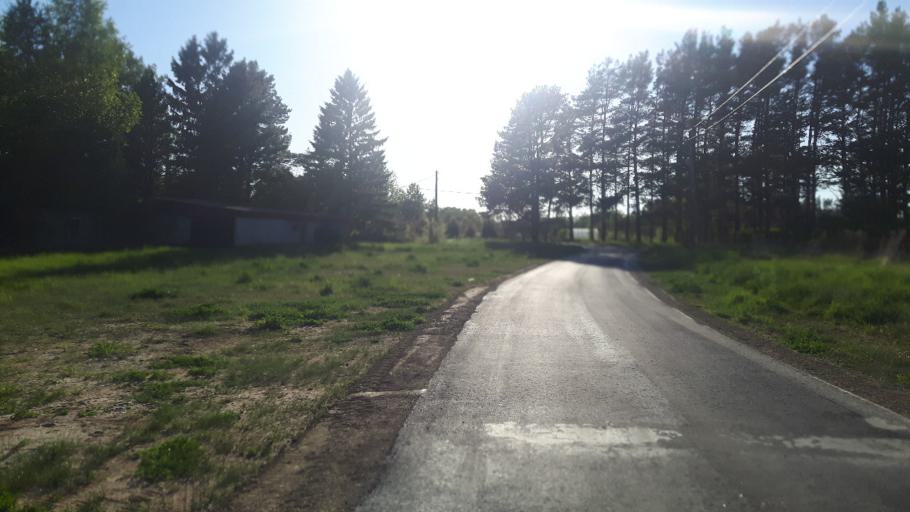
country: EE
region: Ida-Virumaa
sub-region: Kivioli linn
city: Kivioli
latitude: 59.4336
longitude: 26.9636
